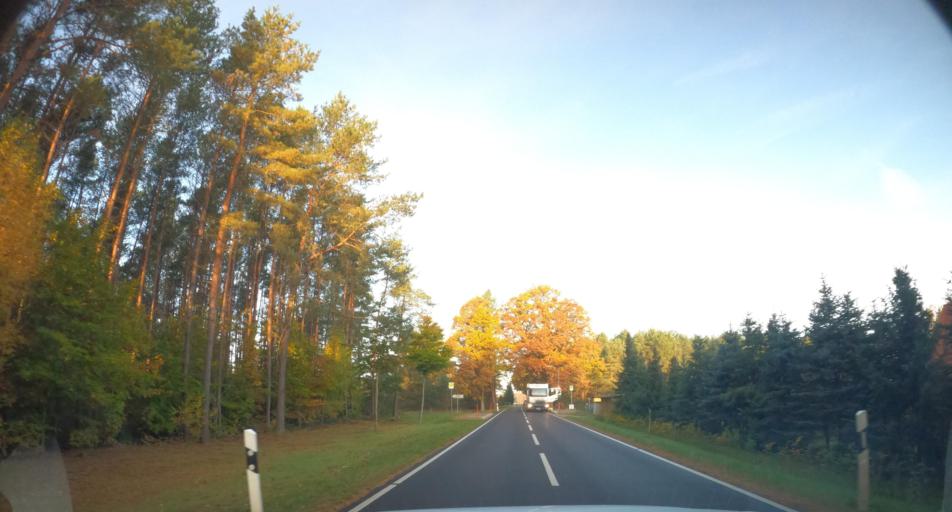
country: DE
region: Mecklenburg-Vorpommern
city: Ahlbeck
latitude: 53.6250
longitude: 14.2280
